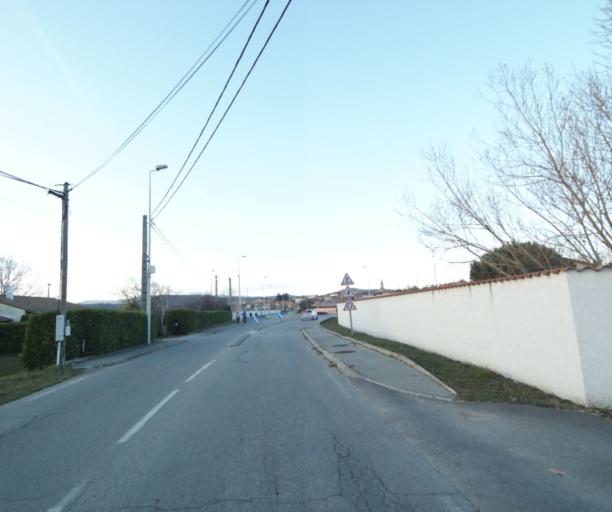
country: FR
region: Rhone-Alpes
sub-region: Departement de l'Ardeche
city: Davezieux
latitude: 45.2481
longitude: 4.7059
